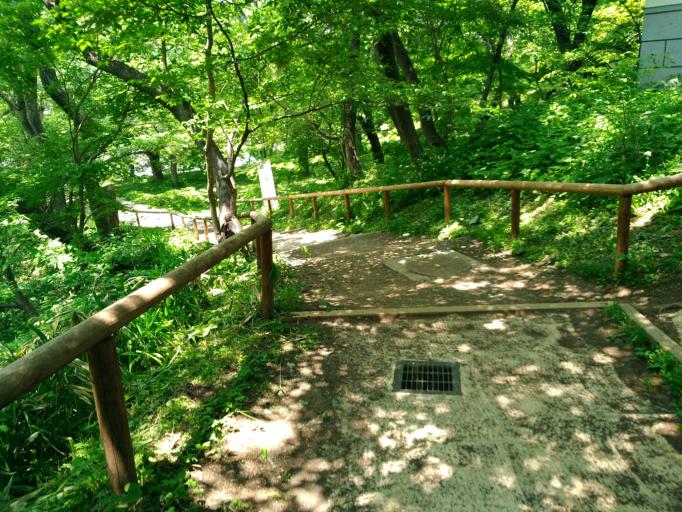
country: JP
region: Nagano
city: Ina
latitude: 35.8336
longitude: 138.0631
